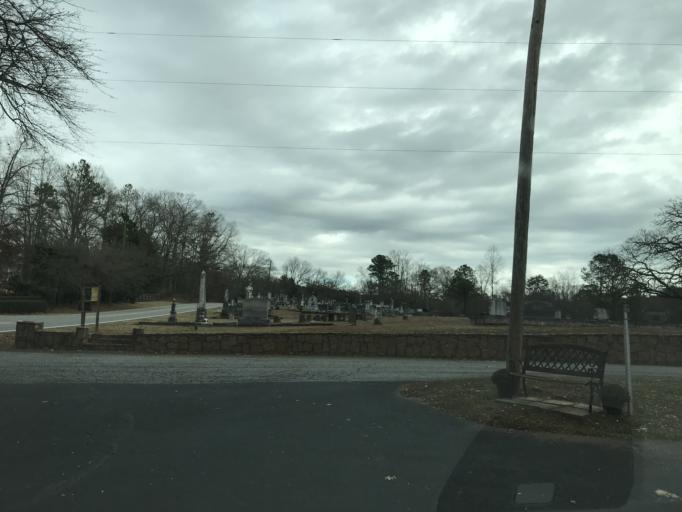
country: US
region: Georgia
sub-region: Fulton County
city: Milton
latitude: 34.1189
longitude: -84.3374
